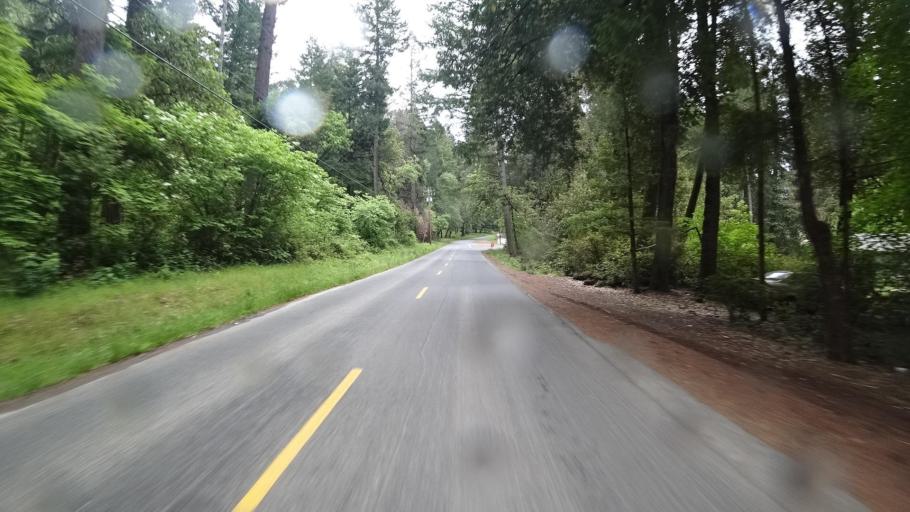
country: US
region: California
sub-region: Humboldt County
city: Willow Creek
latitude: 41.0504
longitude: -123.6669
